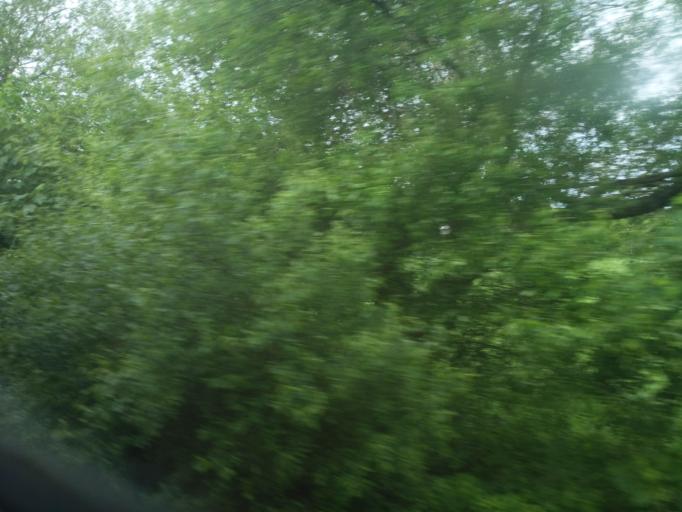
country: GB
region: England
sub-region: Devon
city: Barnstaple
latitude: 51.0311
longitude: -4.0364
